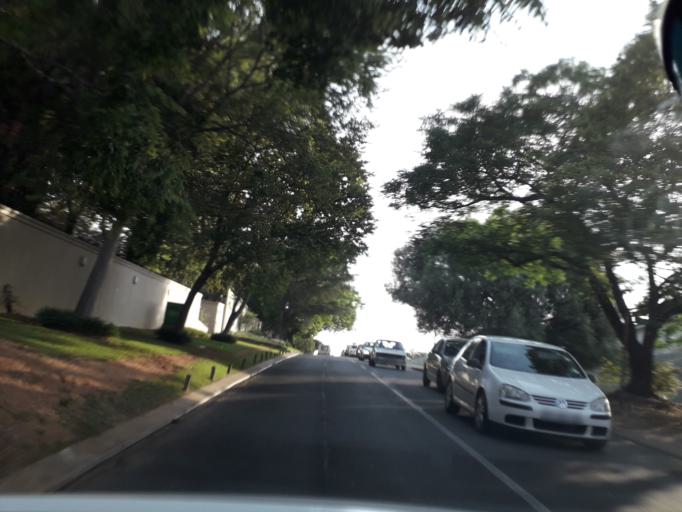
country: ZA
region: Gauteng
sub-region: City of Johannesburg Metropolitan Municipality
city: Diepsloot
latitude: -26.0667
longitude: 27.9884
